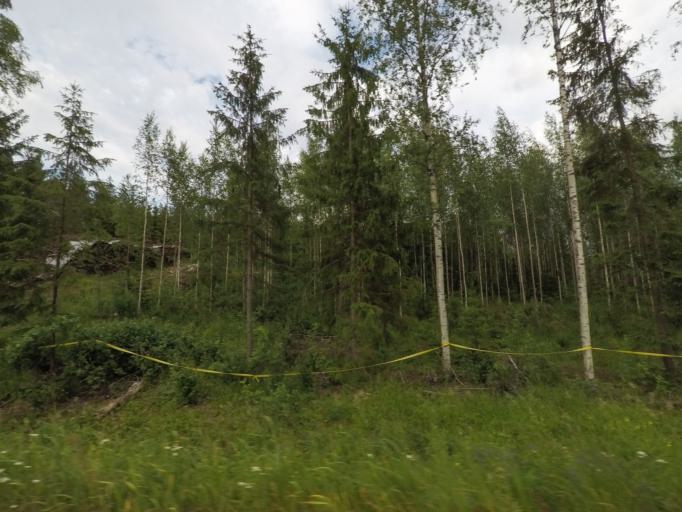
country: FI
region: Paijanne Tavastia
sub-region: Lahti
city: Hollola
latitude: 60.8320
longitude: 25.4908
